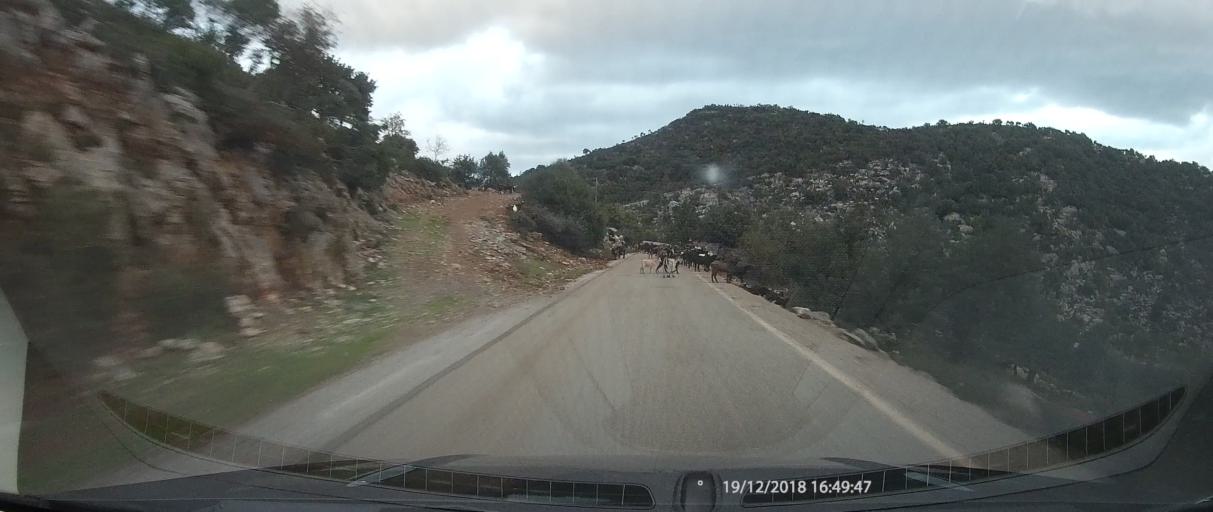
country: GR
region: Peloponnese
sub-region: Nomos Lakonias
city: Sykea
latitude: 36.9493
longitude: 22.9960
